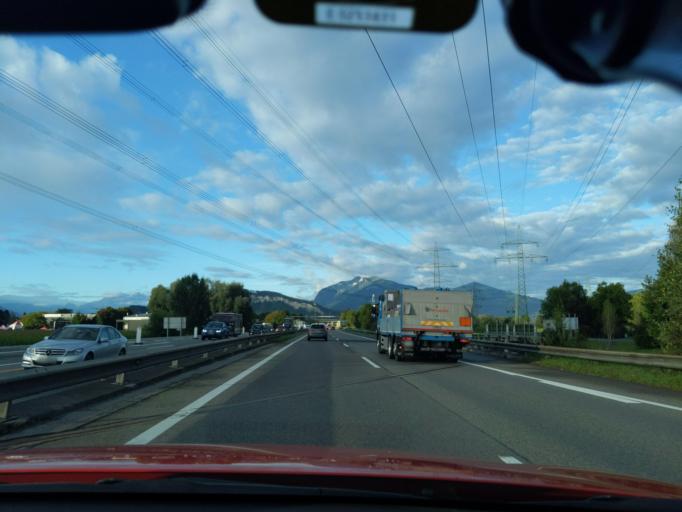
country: AT
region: Vorarlberg
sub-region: Politischer Bezirk Feldkirch
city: Altach
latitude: 47.3652
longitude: 9.6551
